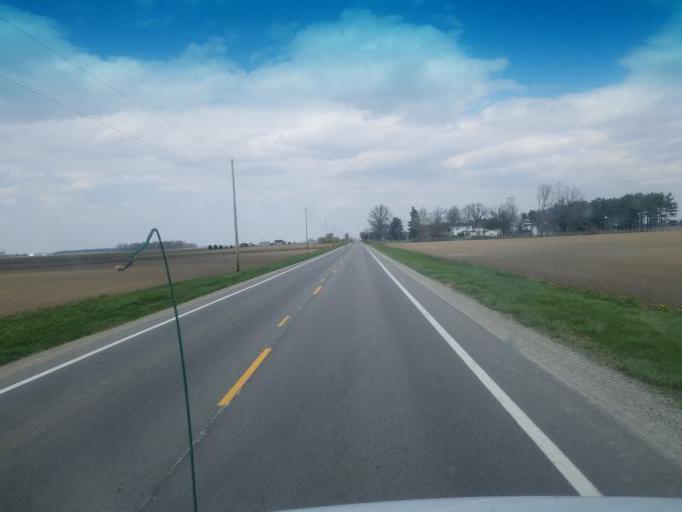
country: US
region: Ohio
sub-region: Wyandot County
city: Upper Sandusky
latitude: 40.8780
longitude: -83.2774
